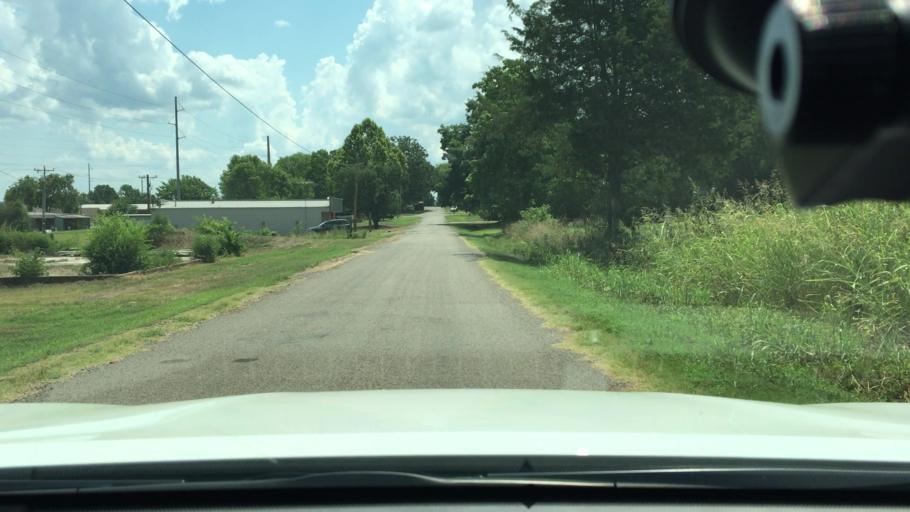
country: US
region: Arkansas
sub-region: Logan County
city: Paris
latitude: 35.2926
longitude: -93.6381
